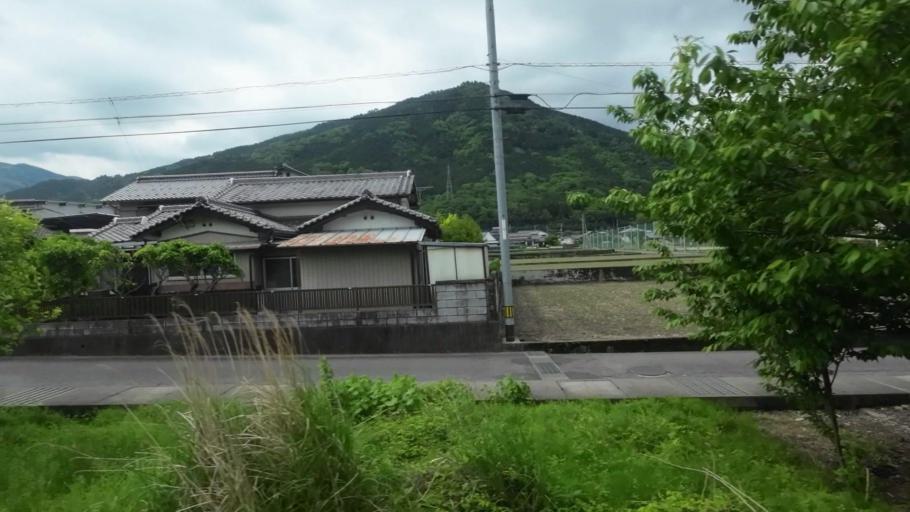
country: JP
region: Tokushima
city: Ikedacho
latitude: 34.0369
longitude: 133.9255
